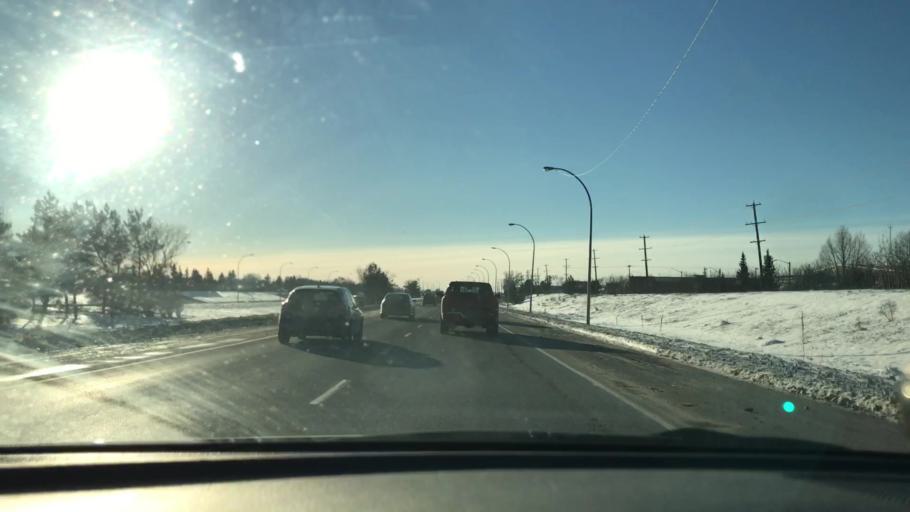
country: CA
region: Alberta
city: Edmonton
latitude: 53.4790
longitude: -113.4669
